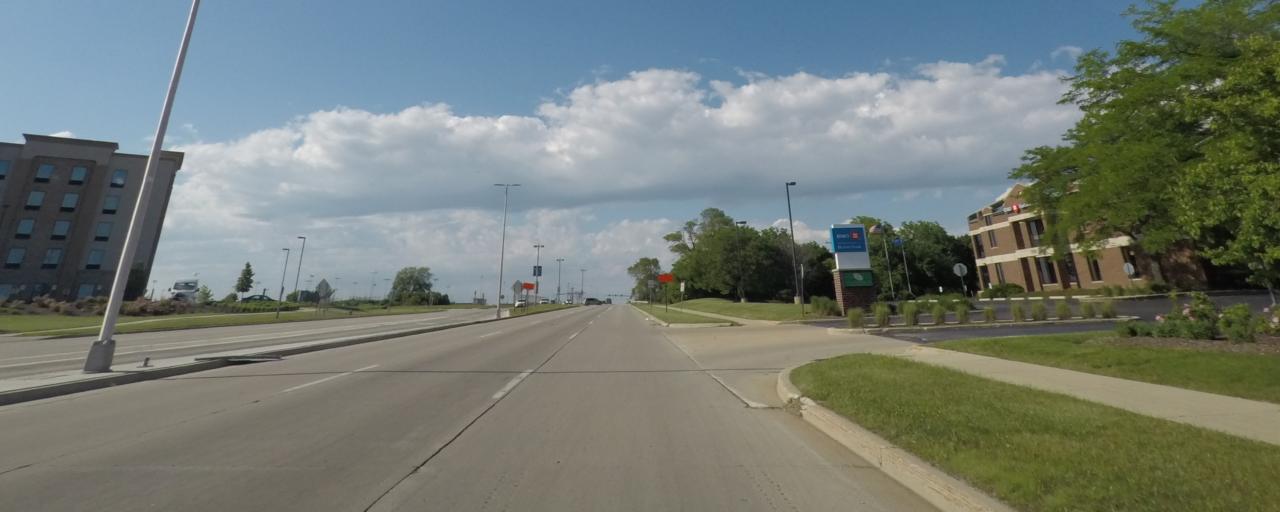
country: US
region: Wisconsin
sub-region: Milwaukee County
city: Greendale
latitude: 42.9165
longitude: -88.0093
